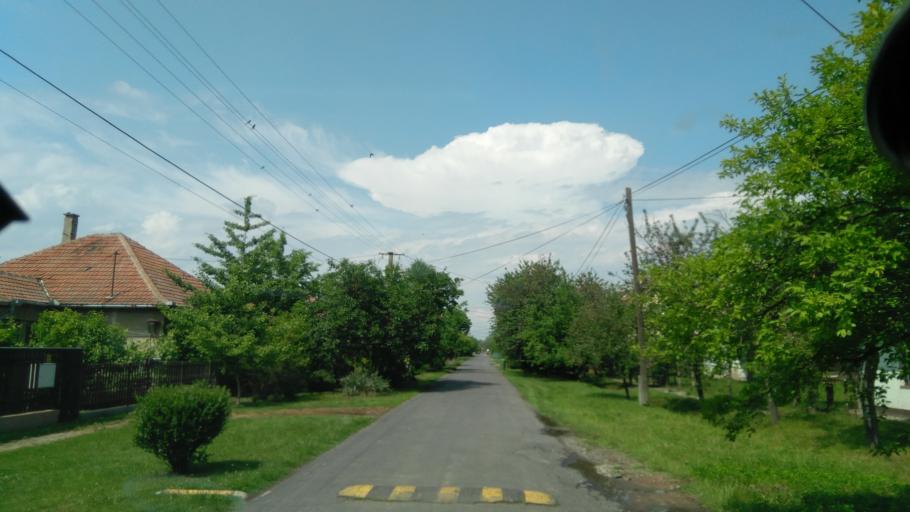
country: HU
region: Bekes
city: Bekes
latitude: 46.7561
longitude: 21.1460
